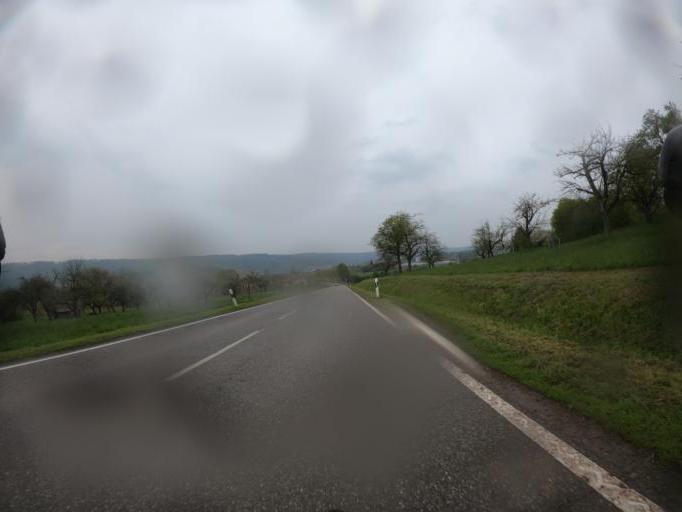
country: DE
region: Baden-Wuerttemberg
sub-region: Karlsruhe Region
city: Muhlacker
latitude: 48.9421
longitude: 8.8772
